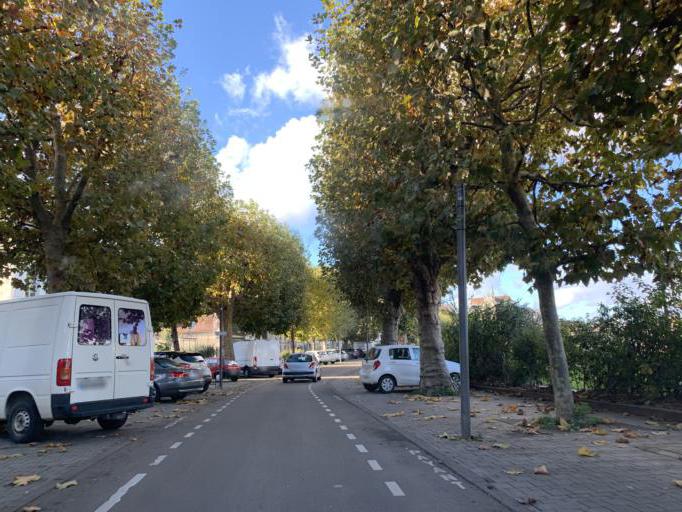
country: FR
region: Bourgogne
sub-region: Departement de l'Yonne
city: Auxerre
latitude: 47.7963
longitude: 3.5760
